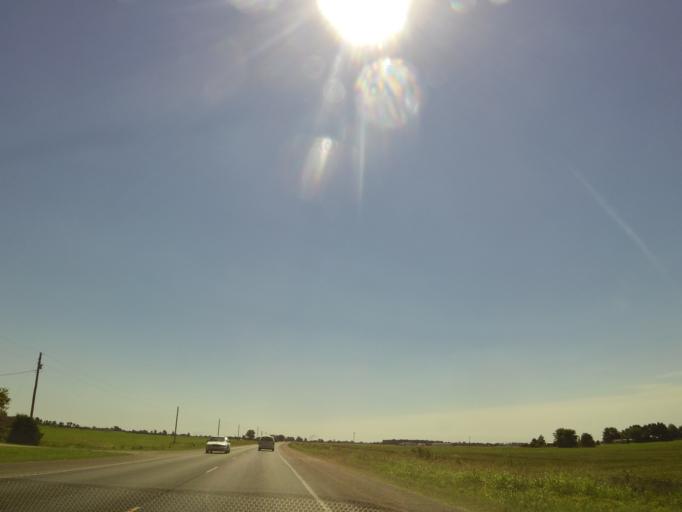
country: US
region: Missouri
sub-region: Dunklin County
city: Campbell
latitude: 36.4920
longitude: -90.0277
